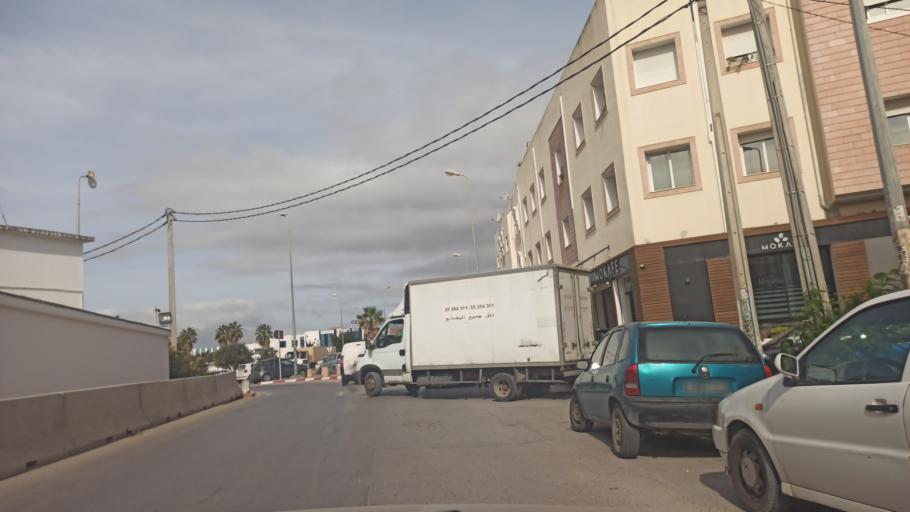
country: TN
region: Tunis
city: La Goulette
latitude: 36.8491
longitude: 10.2603
